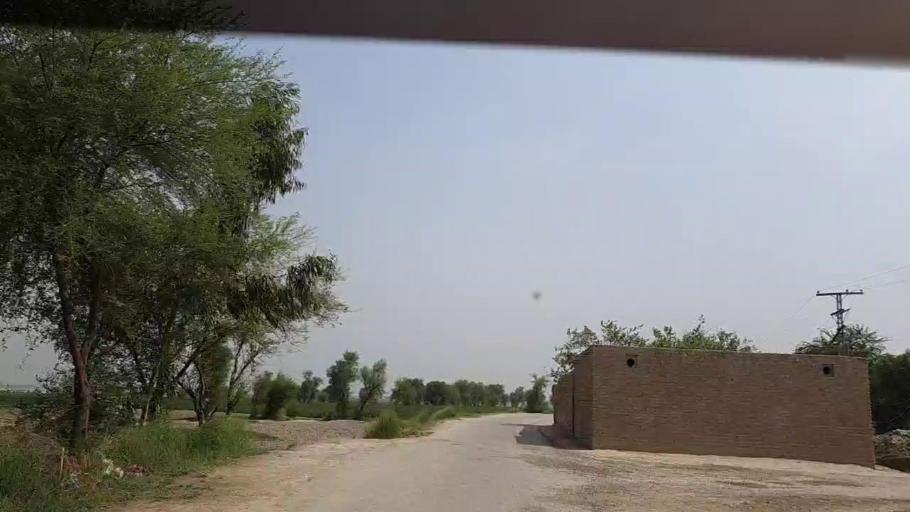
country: PK
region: Sindh
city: Khairpur Nathan Shah
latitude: 27.0598
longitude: 67.6864
